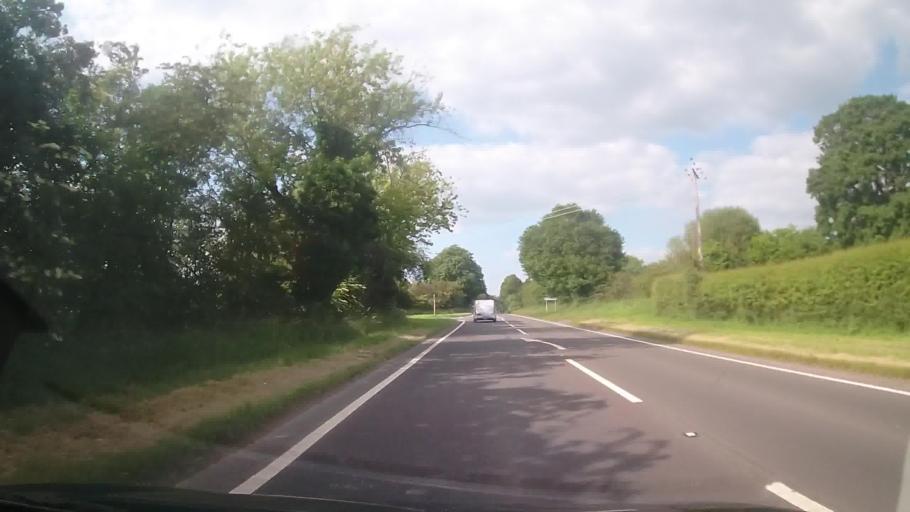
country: GB
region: England
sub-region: Shropshire
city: Church Stretton
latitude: 52.5492
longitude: -2.7916
